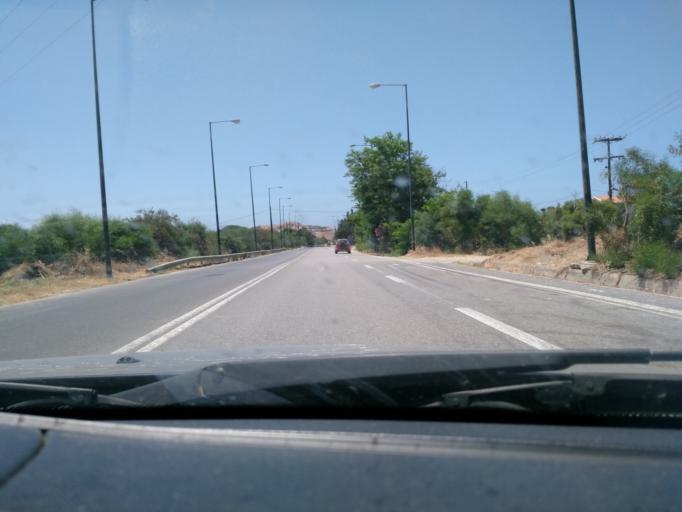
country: GR
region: Crete
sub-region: Nomos Rethymnis
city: Panormos
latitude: 35.4148
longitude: 24.7004
